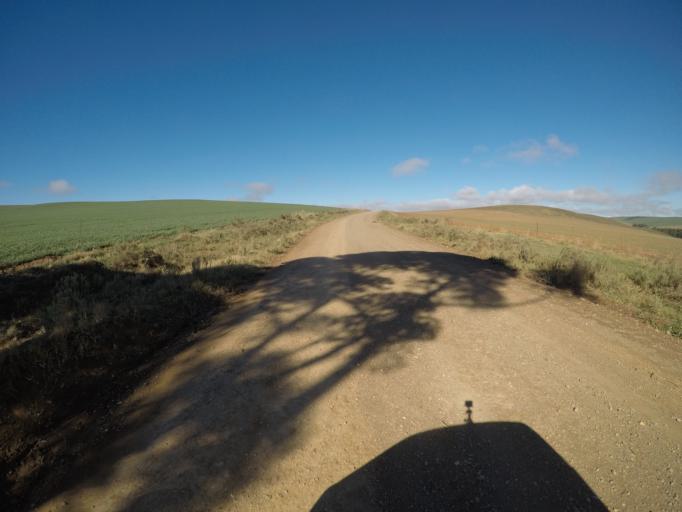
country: ZA
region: Western Cape
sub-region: Overberg District Municipality
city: Caledon
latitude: -34.1119
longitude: 19.7093
